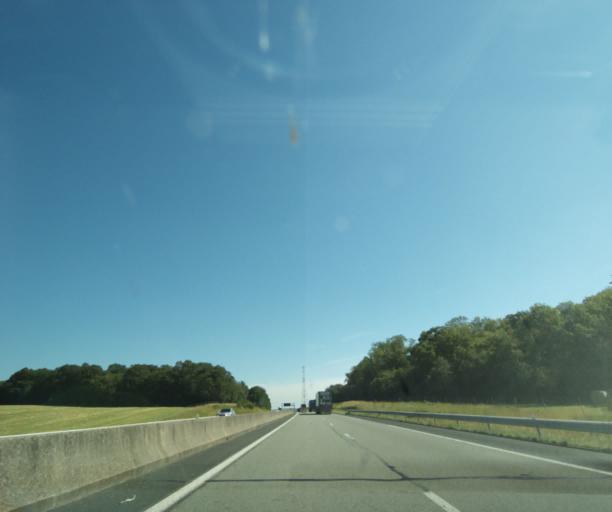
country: FR
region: Lorraine
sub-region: Departement des Vosges
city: Lamarche
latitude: 48.1113
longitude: 5.6576
